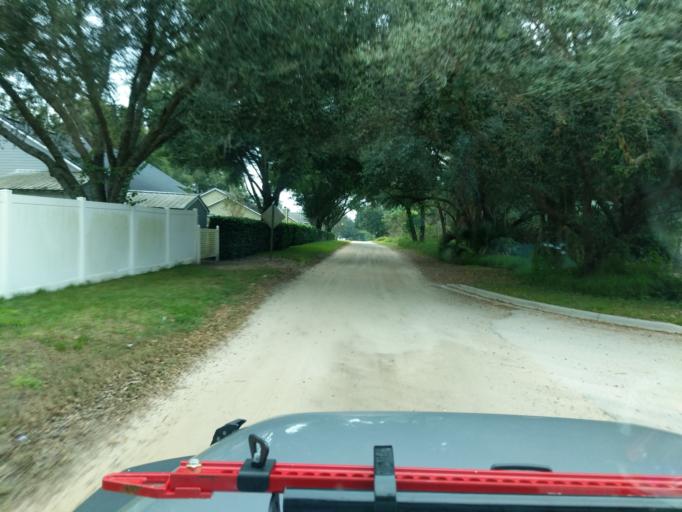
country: US
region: Florida
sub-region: Orange County
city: Oakland
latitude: 28.5579
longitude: -81.6246
